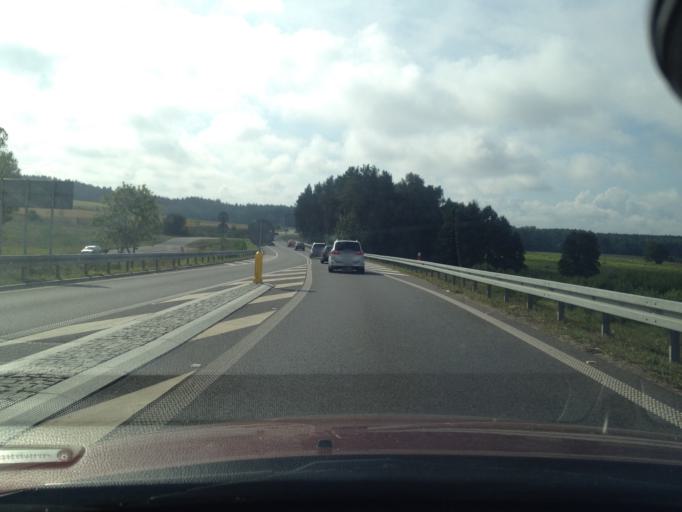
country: PL
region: West Pomeranian Voivodeship
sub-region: Powiat goleniowski
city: Przybiernow
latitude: 53.8441
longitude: 14.7467
